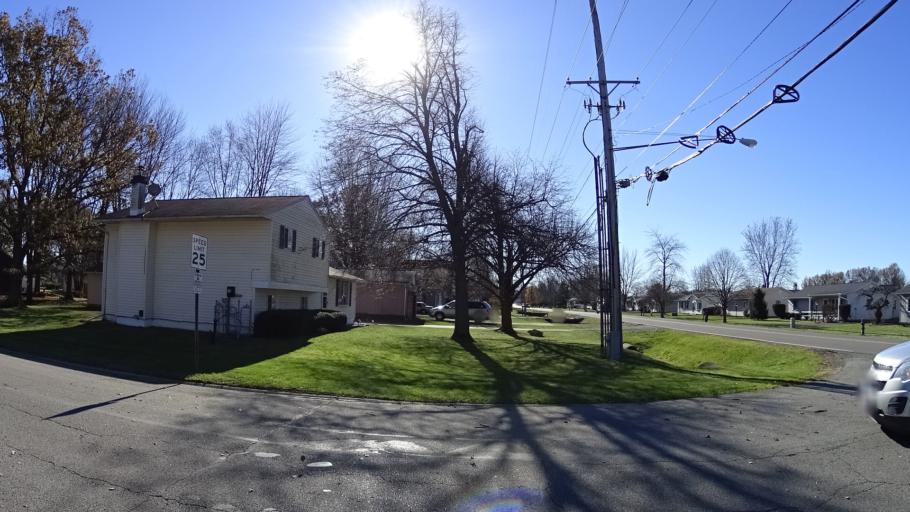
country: US
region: Ohio
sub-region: Lorain County
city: Elyria
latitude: 41.3478
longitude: -82.0780
